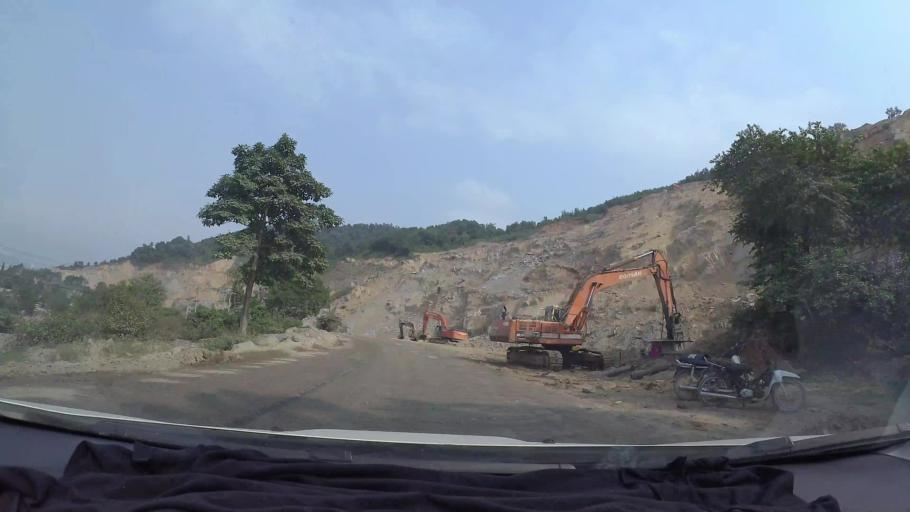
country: VN
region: Da Nang
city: Lien Chieu
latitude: 16.0379
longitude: 108.1542
